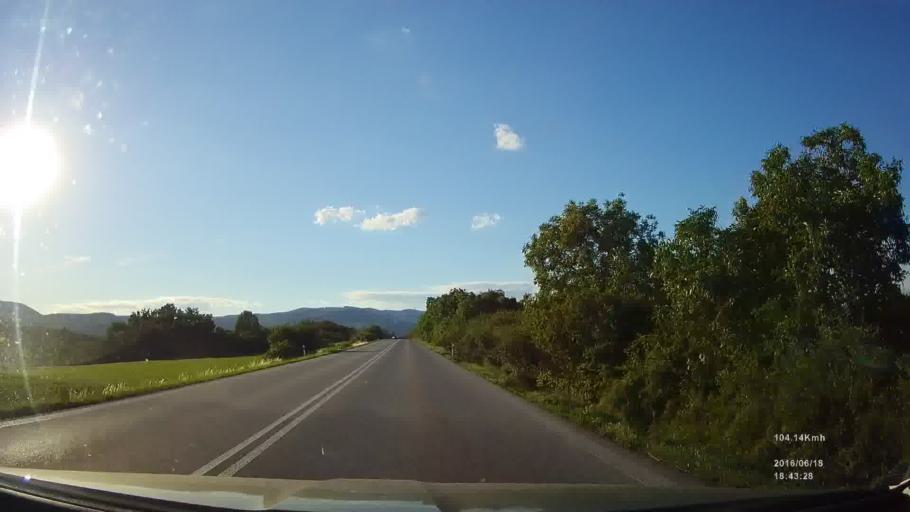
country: SK
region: Kosicky
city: Secovce
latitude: 48.7190
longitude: 21.6113
